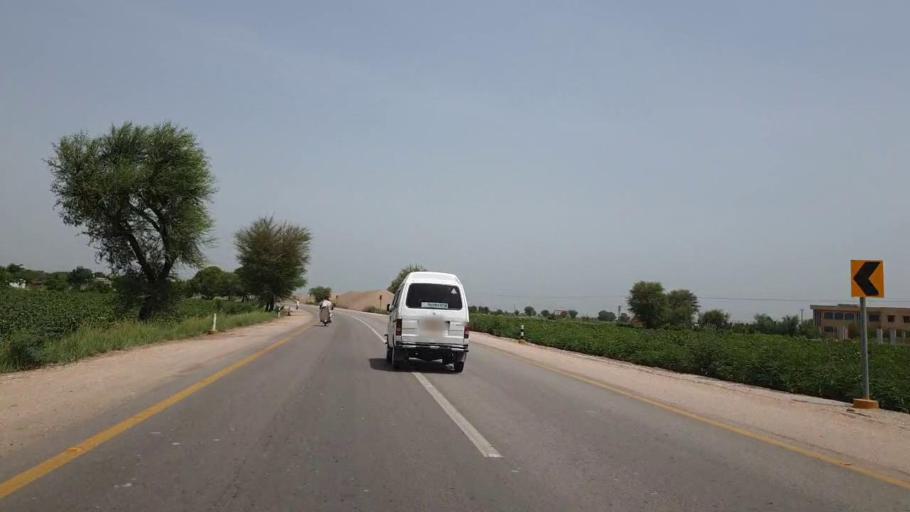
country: PK
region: Sindh
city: Shahpur Chakar
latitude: 26.1621
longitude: 68.6302
